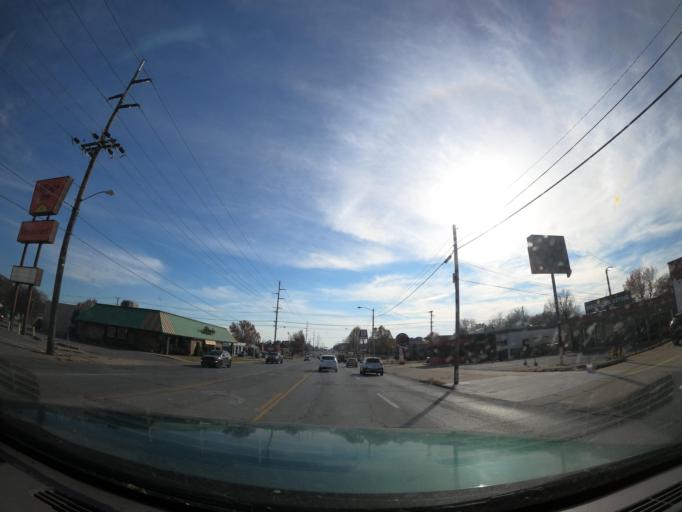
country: US
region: Oklahoma
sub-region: Tulsa County
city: Tulsa
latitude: 36.1231
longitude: -95.9403
